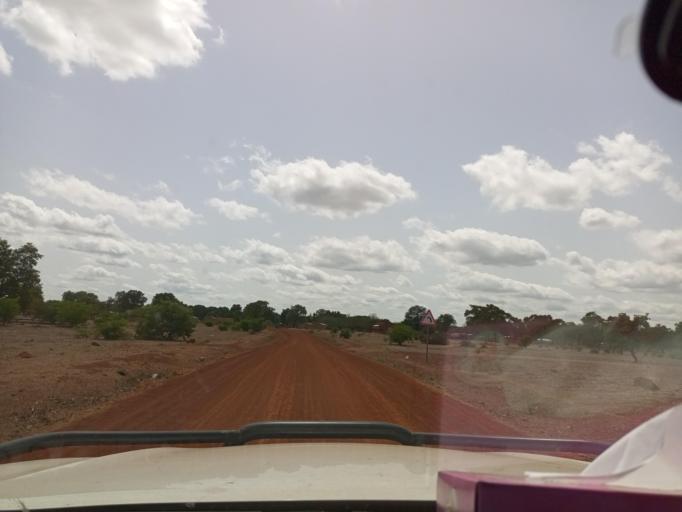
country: ML
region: Sikasso
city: Kolondieba
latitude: 11.5939
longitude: -6.6660
